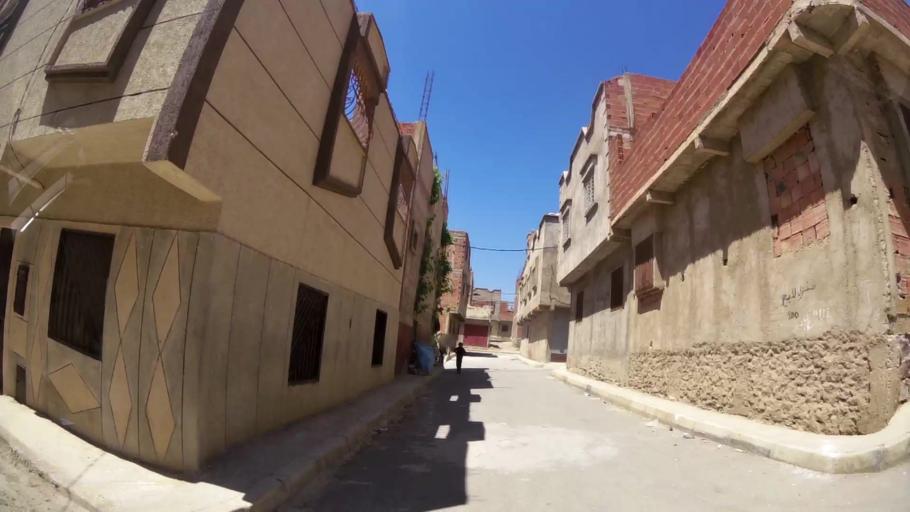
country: MA
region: Oriental
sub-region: Oujda-Angad
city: Oujda
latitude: 34.6801
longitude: -1.9581
